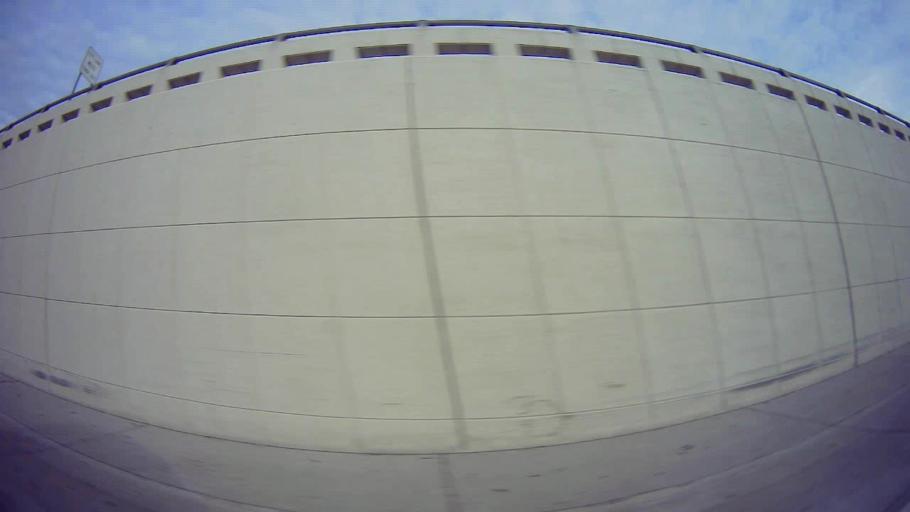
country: US
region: Michigan
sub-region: Wayne County
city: Redford
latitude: 42.3840
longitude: -83.3256
